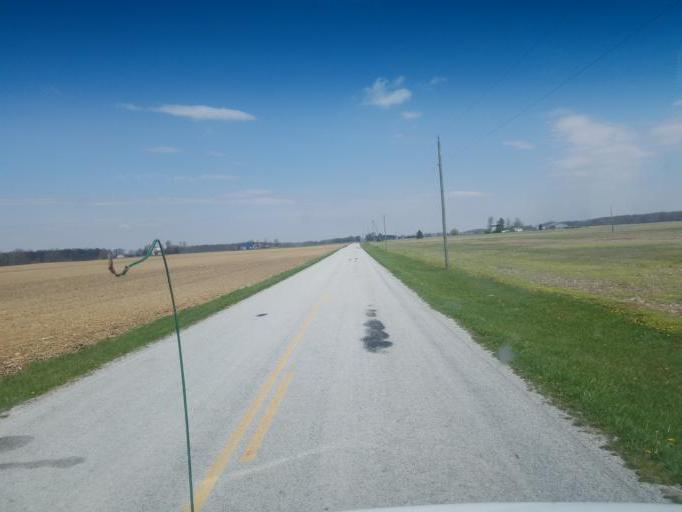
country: US
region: Ohio
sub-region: Hardin County
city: Forest
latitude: 40.7170
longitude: -83.5380
